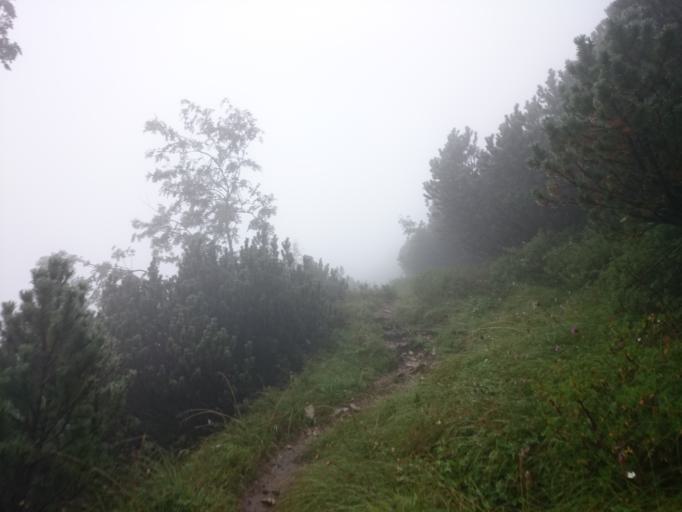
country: AT
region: Tyrol
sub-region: Politischer Bezirk Innsbruck Land
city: Absam
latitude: 47.4111
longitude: 11.5028
